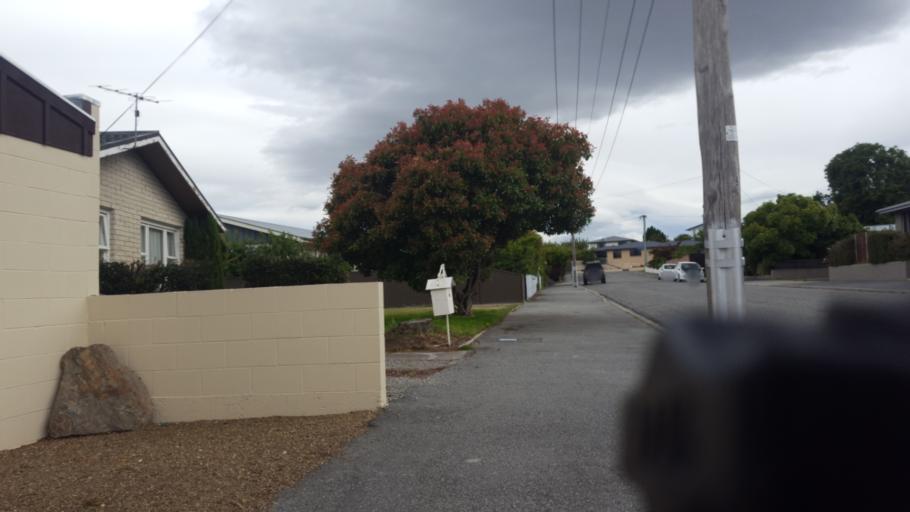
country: NZ
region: Otago
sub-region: Queenstown-Lakes District
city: Wanaka
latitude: -45.2520
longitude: 169.3971
